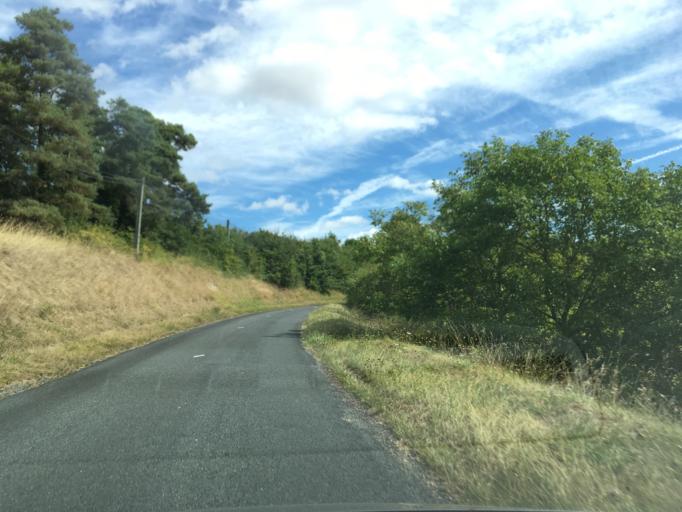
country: FR
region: Haute-Normandie
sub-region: Departement de l'Eure
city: Heudreville-sur-Eure
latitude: 49.1314
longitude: 1.2175
